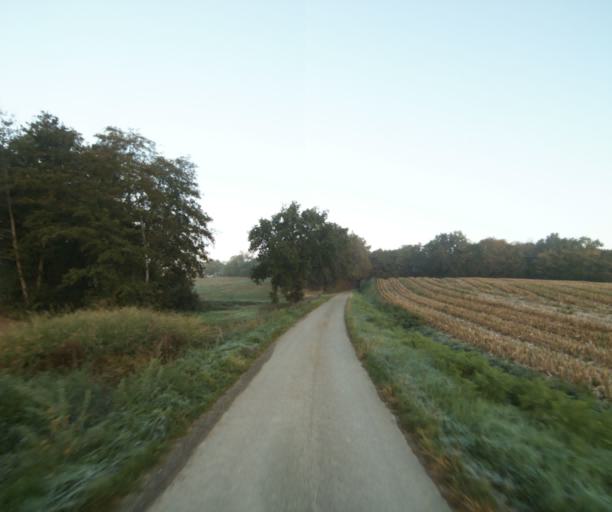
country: FR
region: Midi-Pyrenees
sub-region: Departement du Gers
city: Vic-Fezensac
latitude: 43.7927
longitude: 0.2333
